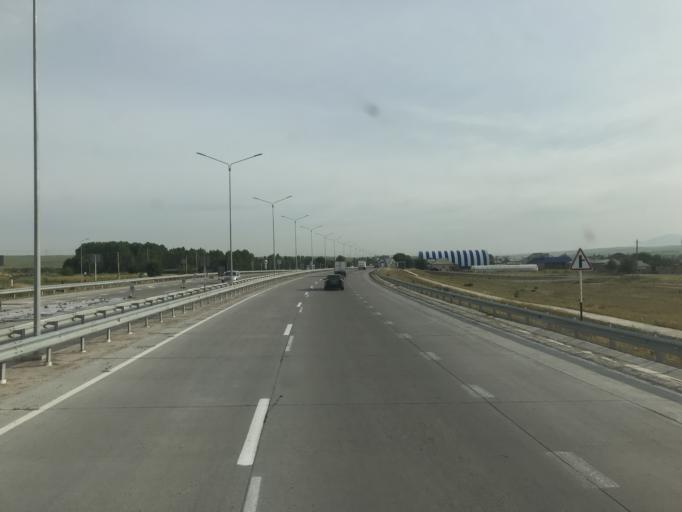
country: KZ
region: Ongtustik Qazaqstan
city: Qazyqurt
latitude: 41.7920
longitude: 69.3925
